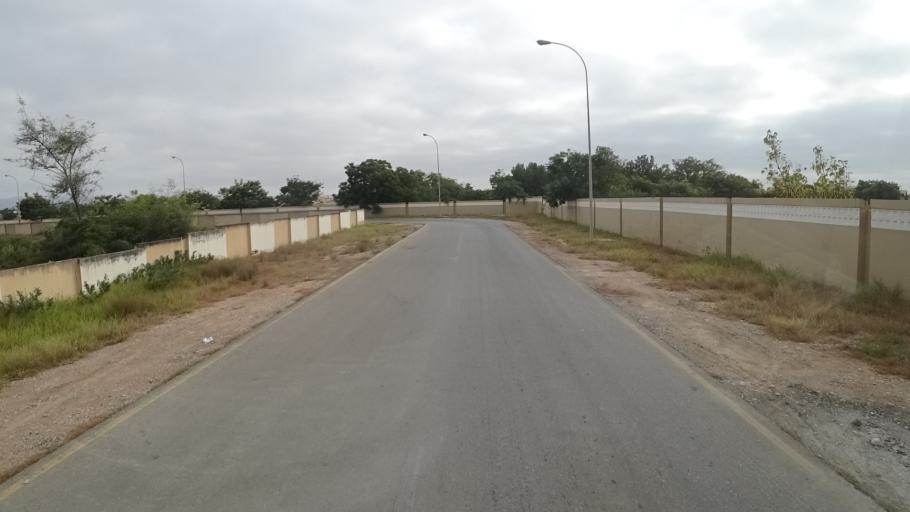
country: OM
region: Zufar
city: Salalah
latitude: 17.0067
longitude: 54.0467
